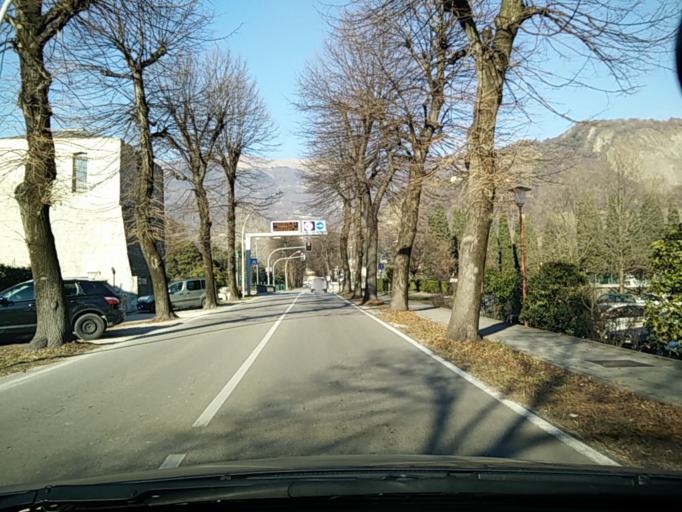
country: IT
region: Veneto
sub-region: Provincia di Treviso
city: Vittorio Veneto
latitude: 45.9939
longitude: 12.2960
